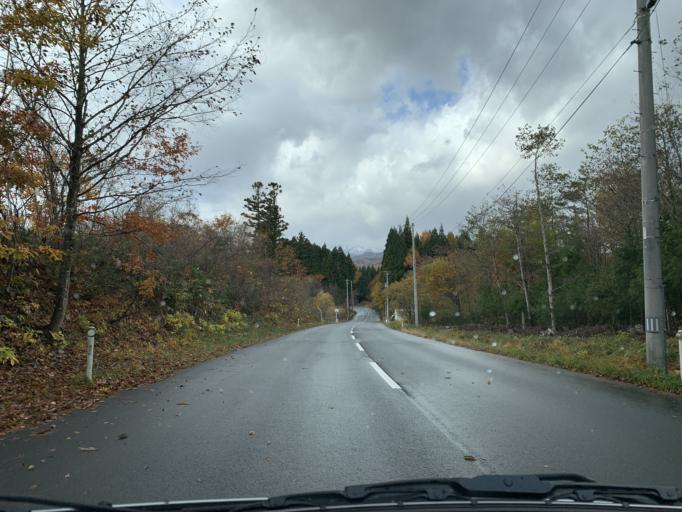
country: JP
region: Iwate
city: Mizusawa
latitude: 39.1121
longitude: 140.9606
